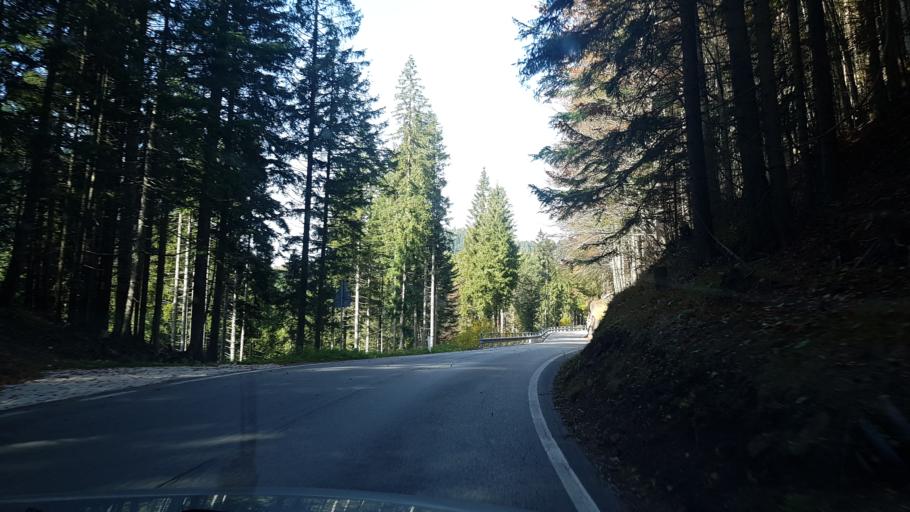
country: IT
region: Veneto
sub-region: Provincia di Belluno
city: Candide
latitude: 46.6445
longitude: 12.4523
